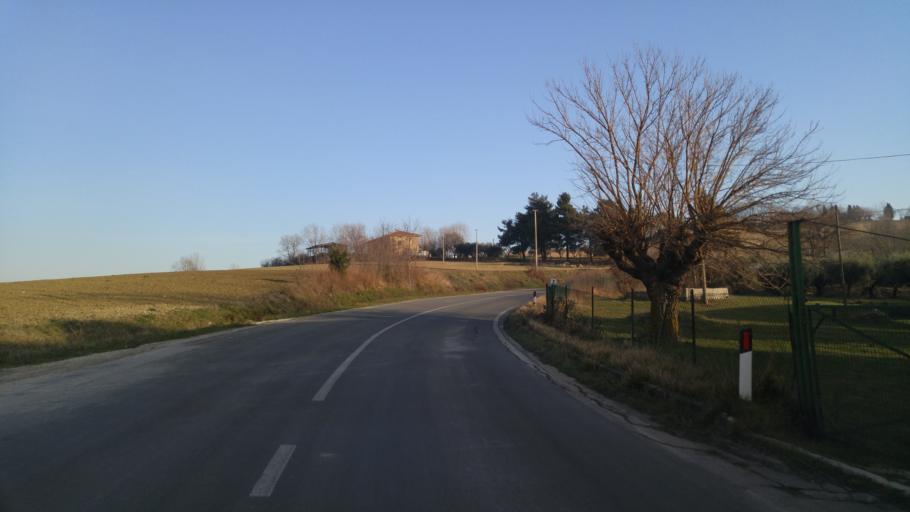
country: IT
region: The Marches
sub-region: Provincia di Pesaro e Urbino
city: San Giorgio di Pesaro
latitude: 43.7098
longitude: 13.0113
